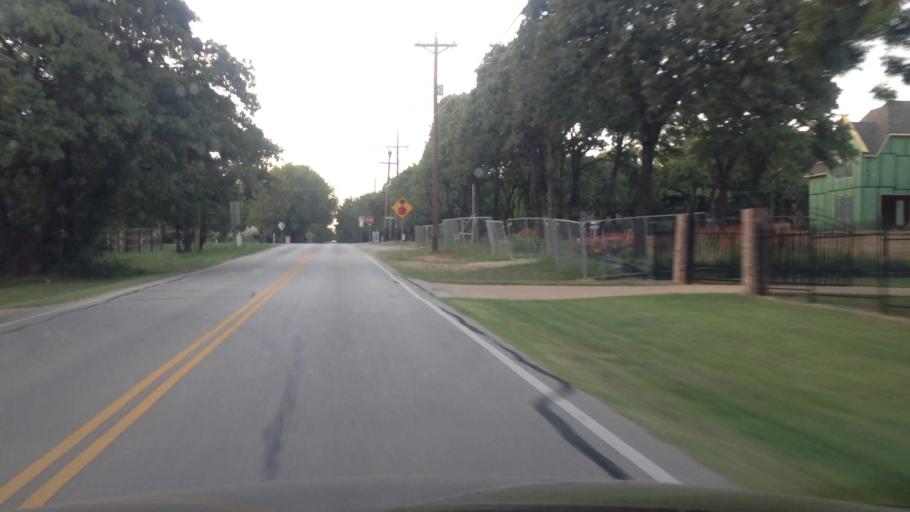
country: US
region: Texas
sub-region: Tarrant County
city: Keller
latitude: 32.9479
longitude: -97.2031
